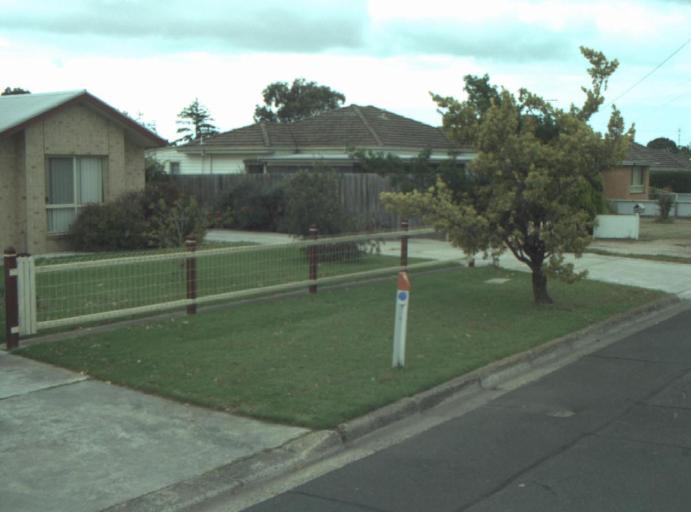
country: AU
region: Victoria
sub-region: Greater Geelong
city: Lara
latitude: -38.0304
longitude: 144.4129
